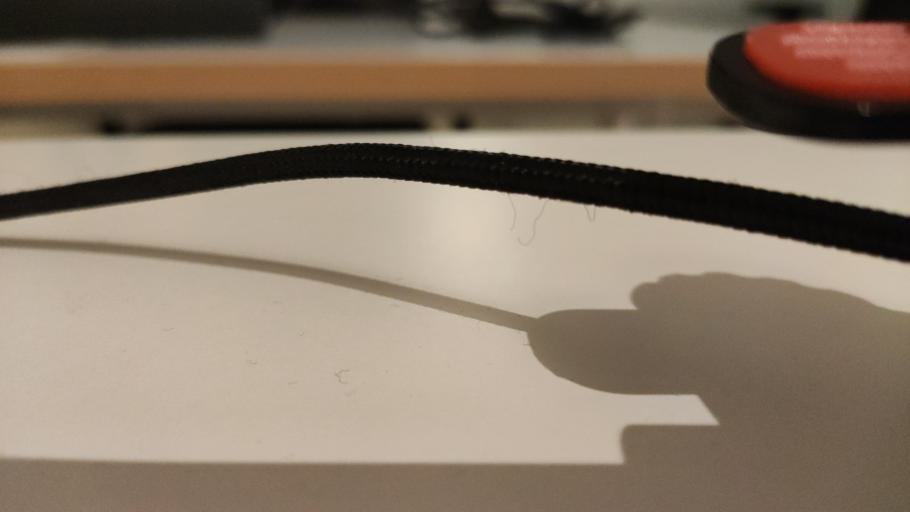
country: RU
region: Moskovskaya
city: Kurovskoye
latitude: 55.5357
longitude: 38.8727
